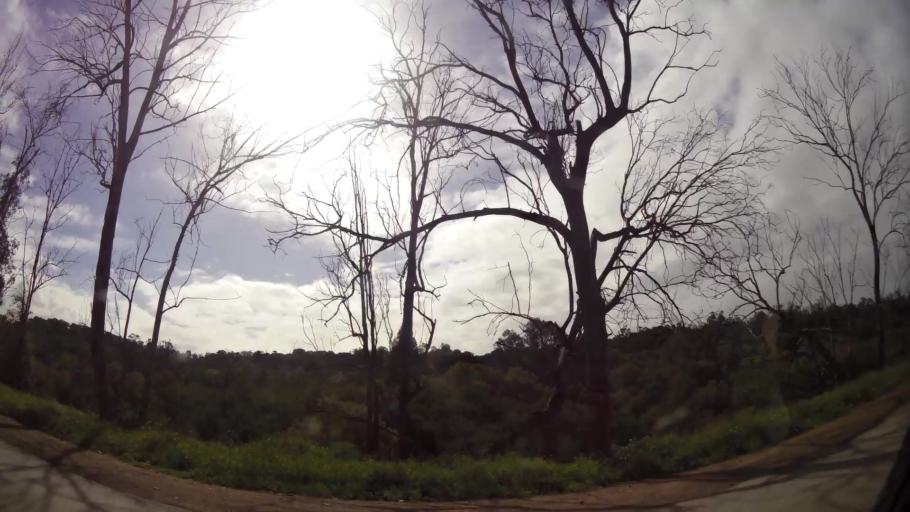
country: MA
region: Grand Casablanca
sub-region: Mohammedia
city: Mohammedia
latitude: 33.6608
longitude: -7.3991
